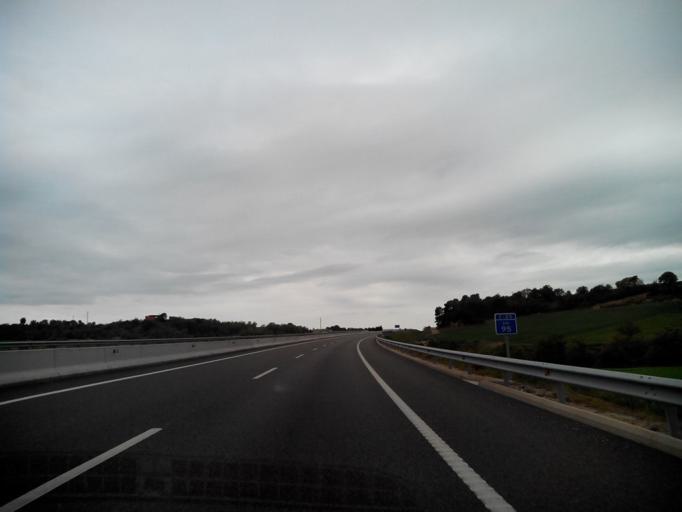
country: ES
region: Catalonia
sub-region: Provincia de Barcelona
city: Pujalt
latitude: 41.7335
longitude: 1.4053
